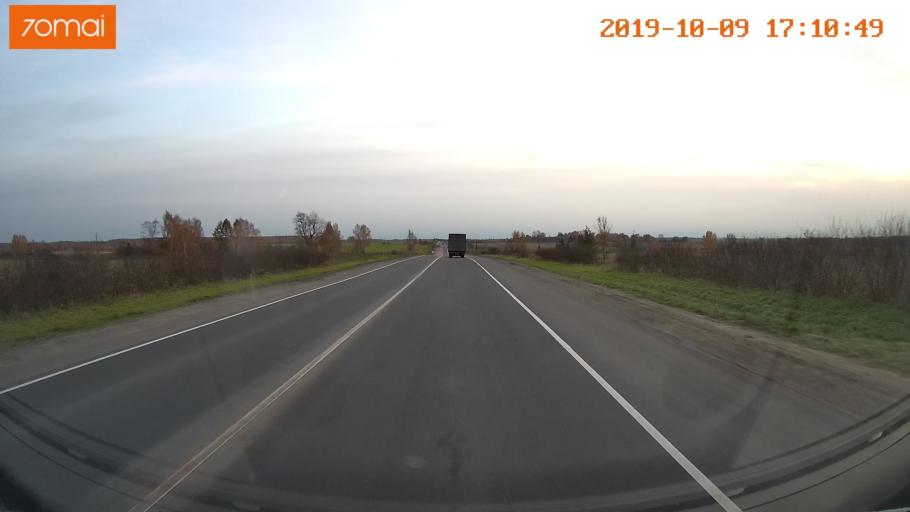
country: RU
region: Ivanovo
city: Privolzhsk
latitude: 57.3507
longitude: 41.2545
